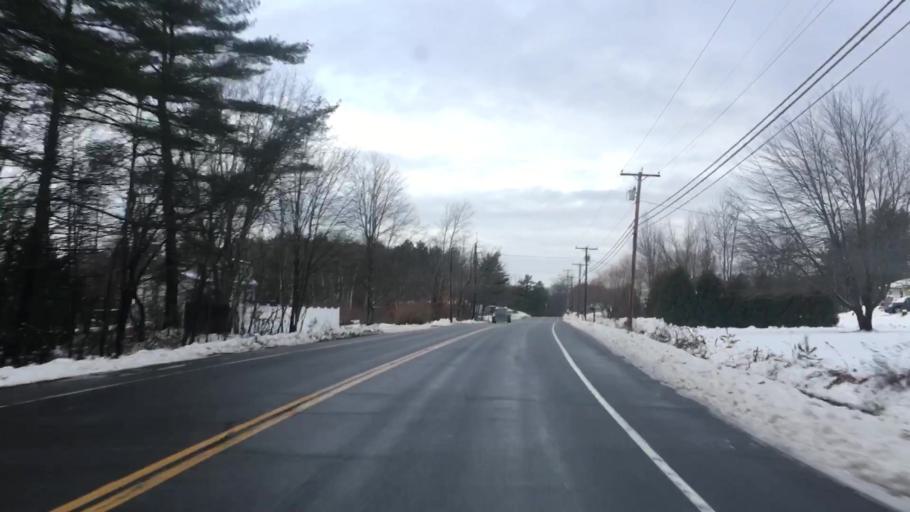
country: US
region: Maine
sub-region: York County
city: Limington
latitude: 43.7340
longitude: -70.6595
